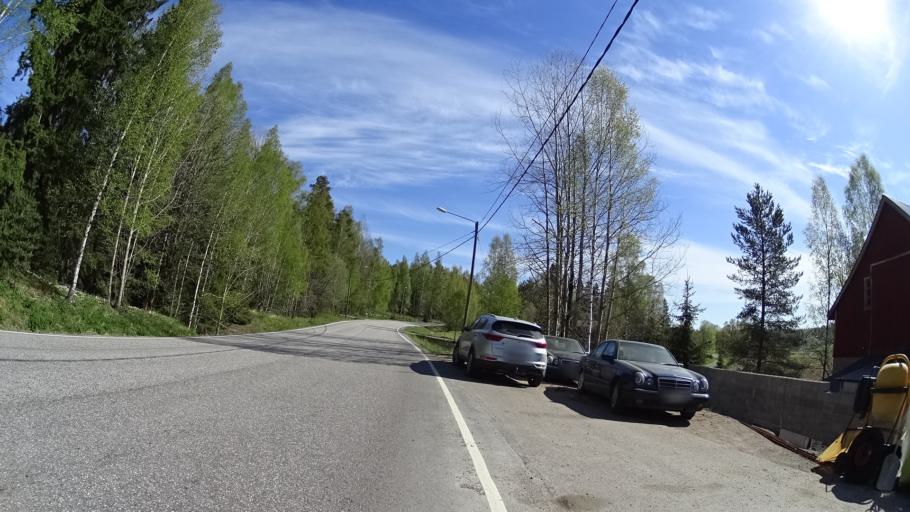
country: FI
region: Uusimaa
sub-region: Helsinki
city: Nurmijaervi
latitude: 60.3959
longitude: 24.8234
